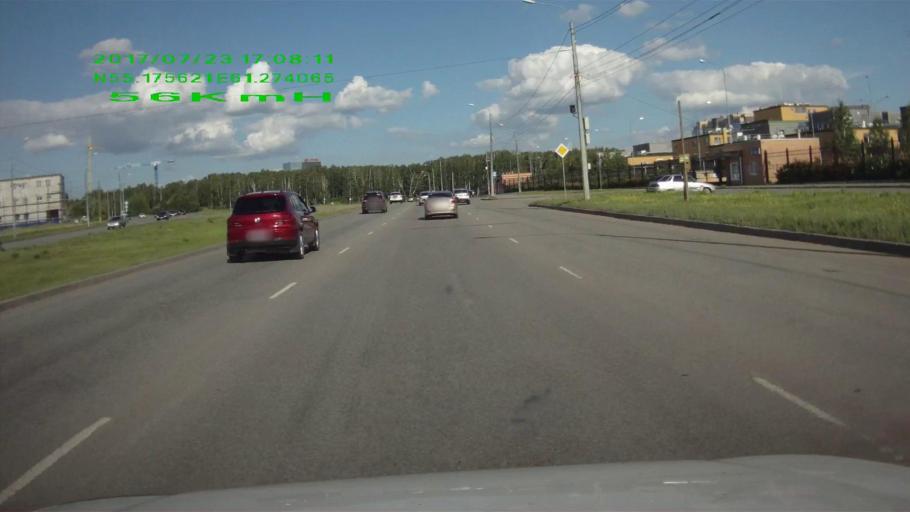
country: RU
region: Chelyabinsk
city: Roshchino
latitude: 55.1755
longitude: 61.2750
